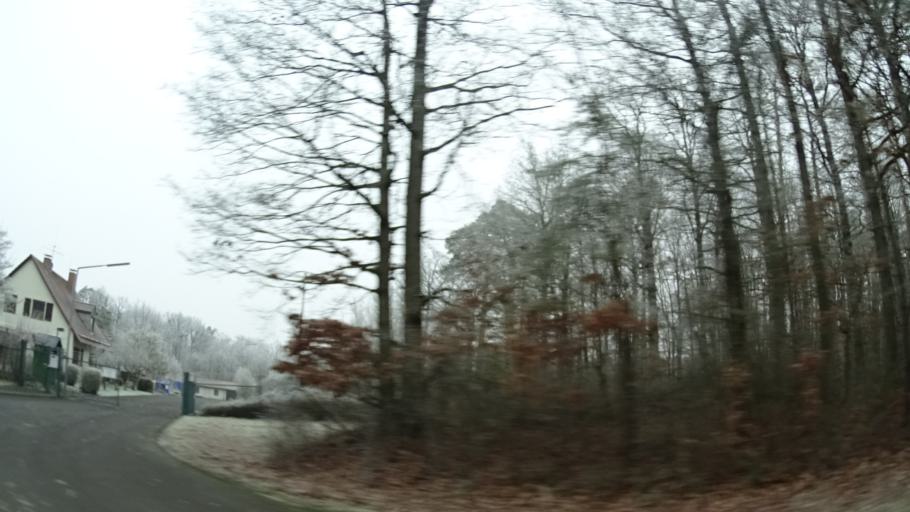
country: DE
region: Bavaria
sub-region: Regierungsbezirk Unterfranken
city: Volkach
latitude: 49.8347
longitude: 10.2402
